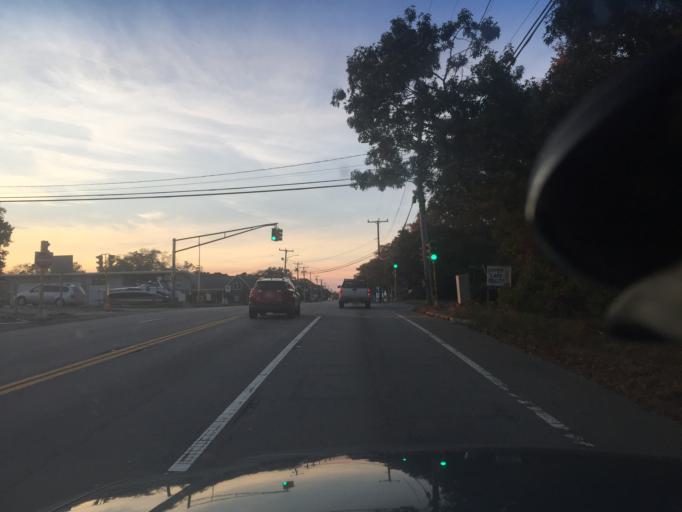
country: US
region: Massachusetts
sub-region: Barnstable County
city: Buzzards Bay
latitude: 41.7492
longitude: -70.6261
